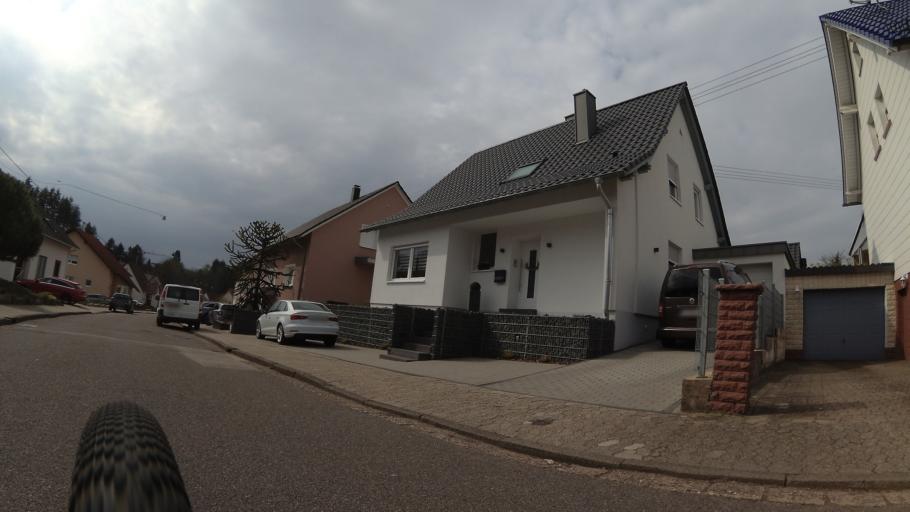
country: DE
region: Saarland
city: Mettlach
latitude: 49.4730
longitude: 6.6156
